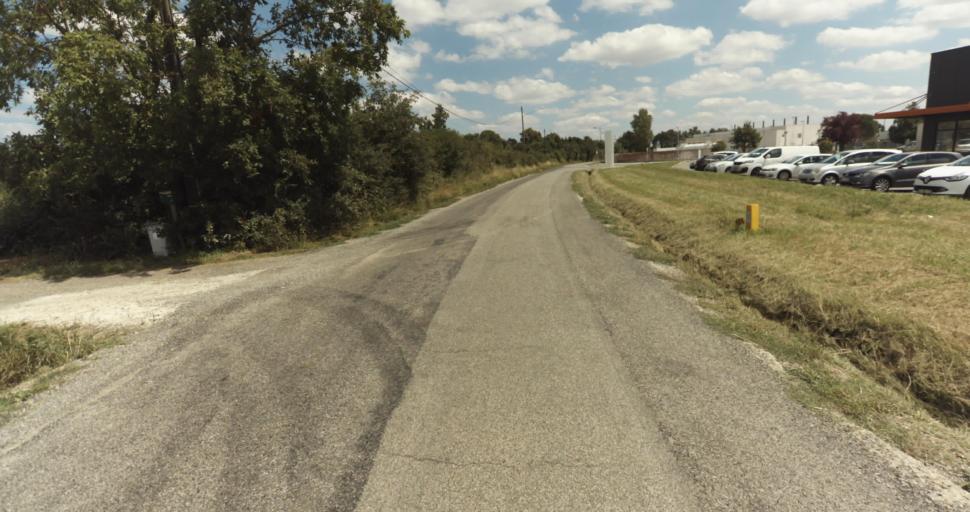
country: FR
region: Midi-Pyrenees
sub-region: Departement de la Haute-Garonne
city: Fontenilles
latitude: 43.5596
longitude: 1.1749
